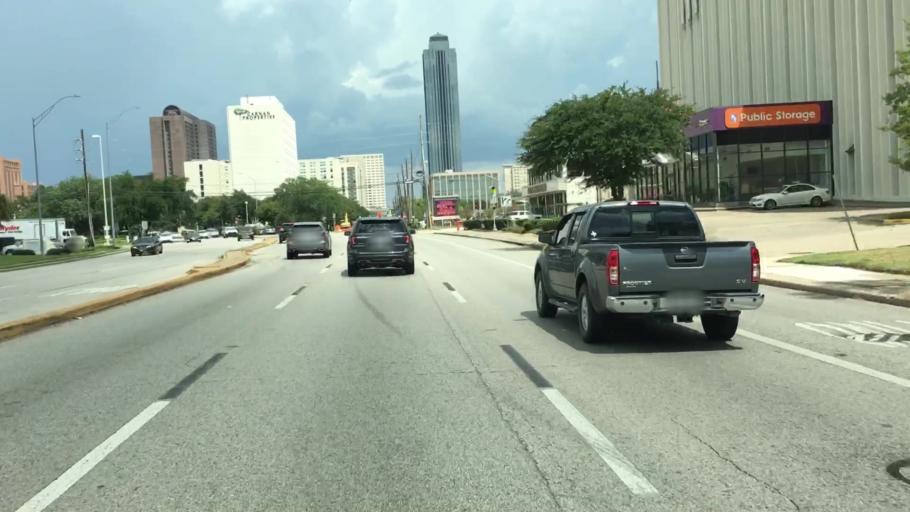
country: US
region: Texas
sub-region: Harris County
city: Bellaire
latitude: 29.7379
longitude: -95.4754
